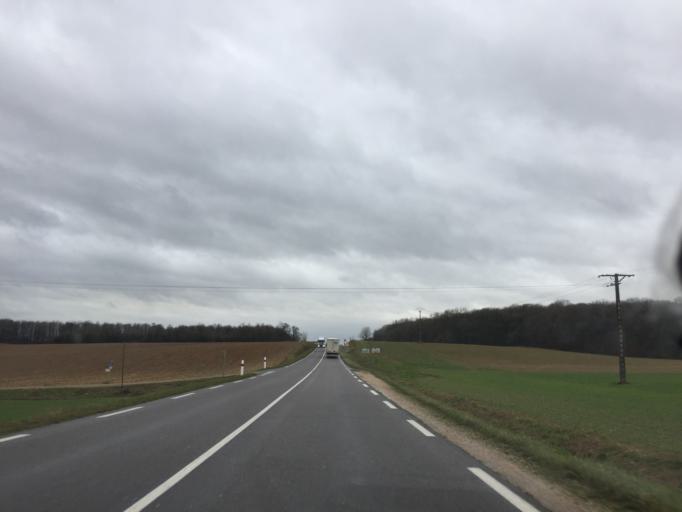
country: FR
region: Franche-Comte
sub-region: Departement du Jura
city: Dole
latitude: 47.1190
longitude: 5.5437
